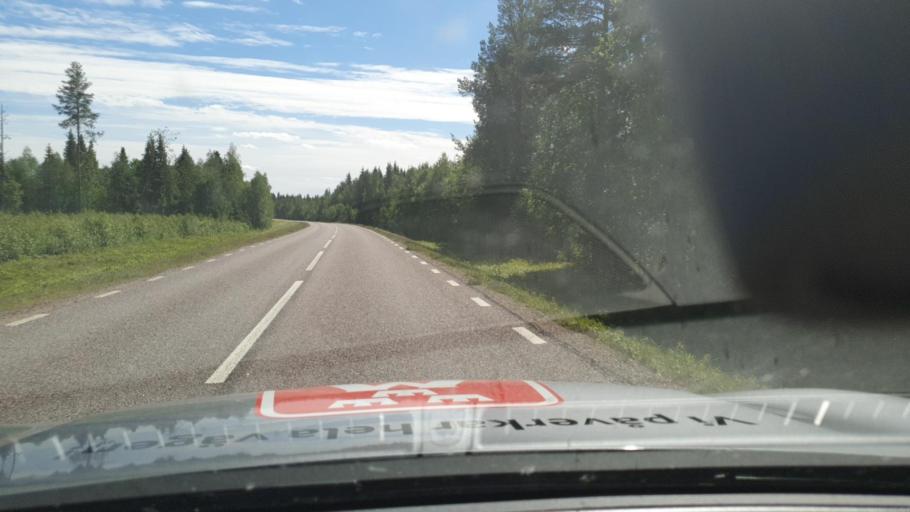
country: FI
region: Lapland
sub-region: Torniolaakso
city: Pello
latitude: 66.9236
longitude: 23.8519
